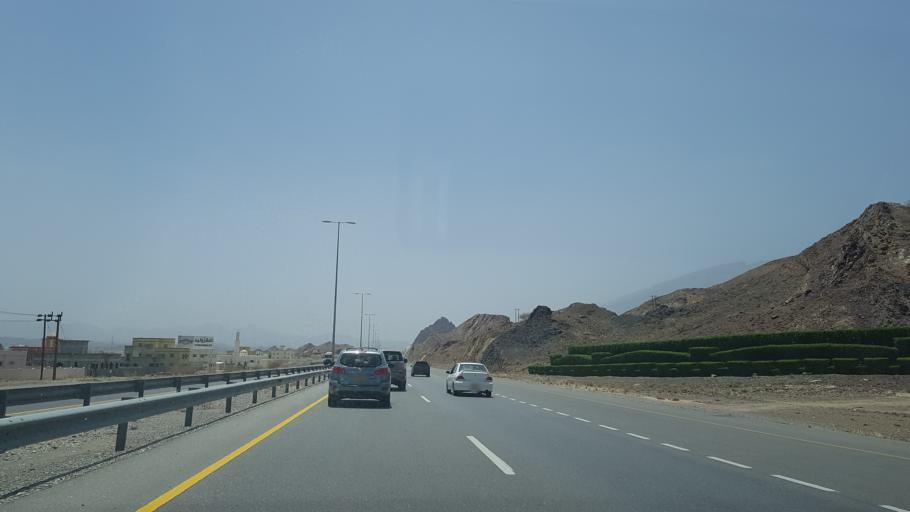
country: OM
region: Muhafazat ad Dakhiliyah
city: Sufalat Sama'il
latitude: 23.3003
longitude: 57.9417
